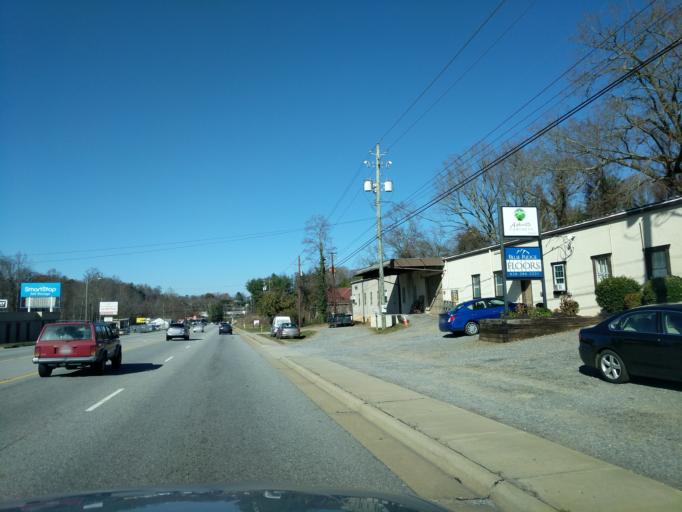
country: US
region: North Carolina
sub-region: Buncombe County
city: Biltmore Forest
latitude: 35.5411
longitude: -82.5208
